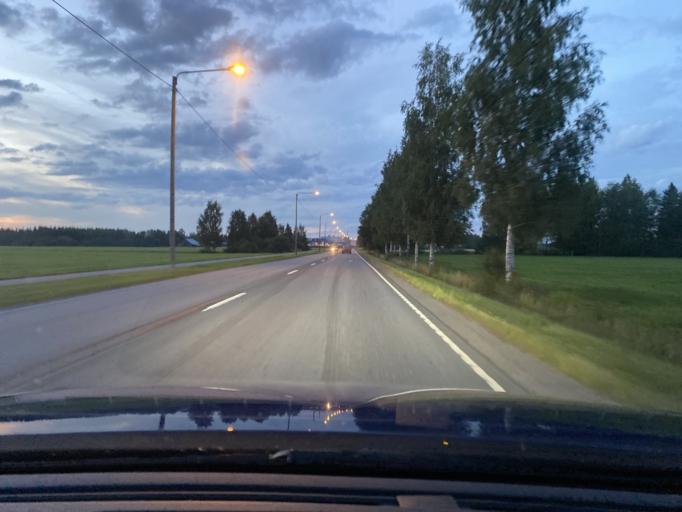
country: FI
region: Southern Ostrobothnia
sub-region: Suupohja
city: Kauhajoki
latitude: 62.4389
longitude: 22.2084
